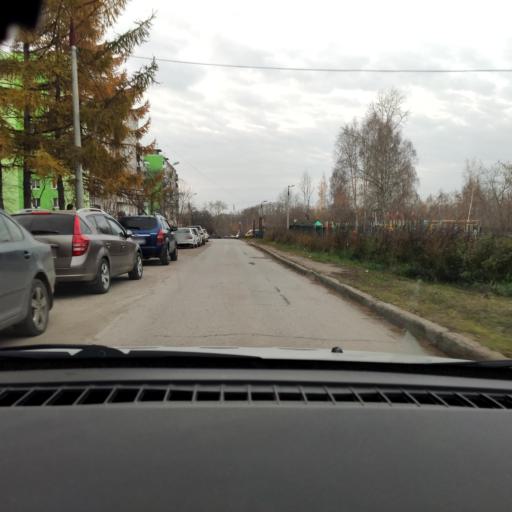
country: RU
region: Perm
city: Perm
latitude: 58.1117
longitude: 56.3802
